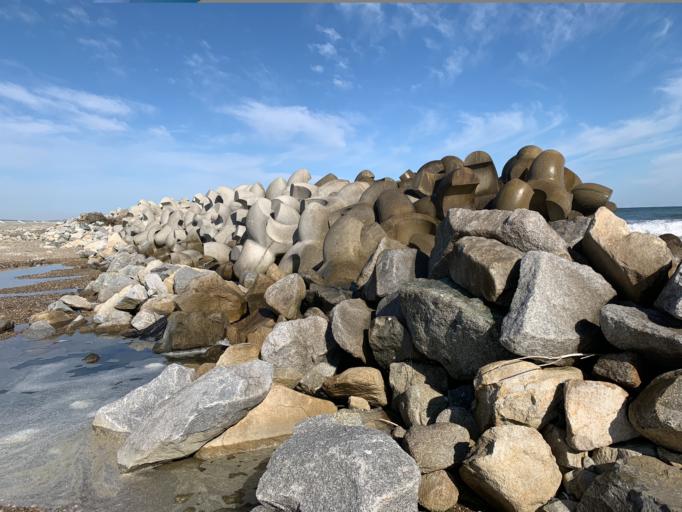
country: JP
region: Miyagi
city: Marumori
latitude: 37.7796
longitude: 140.9879
